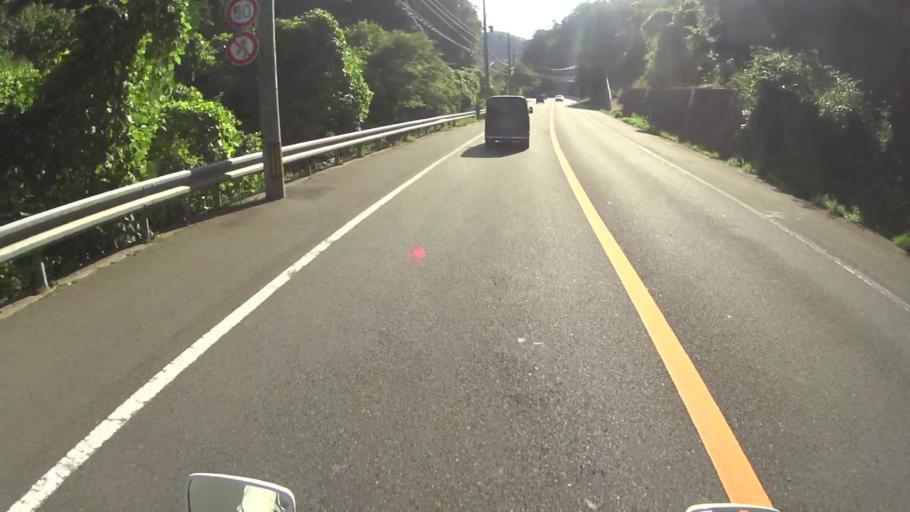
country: JP
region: Kyoto
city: Miyazu
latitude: 35.6617
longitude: 135.0100
